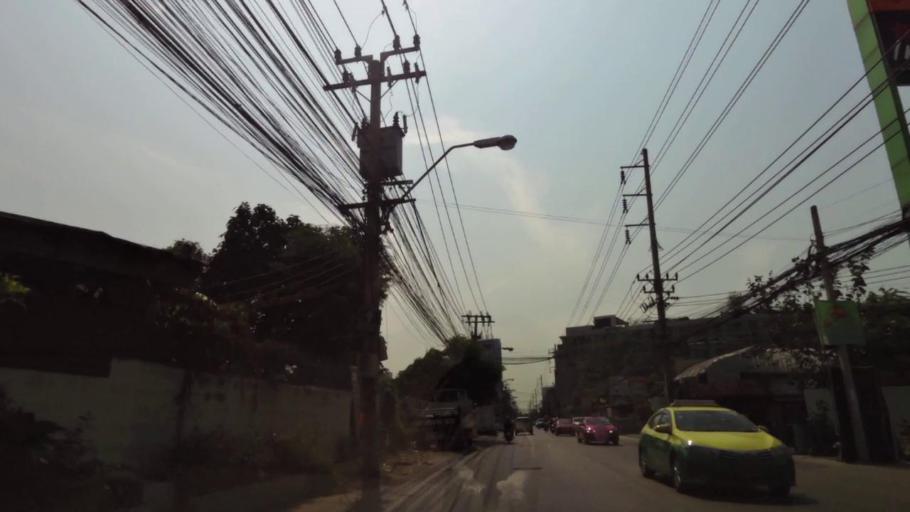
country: TH
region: Bangkok
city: Phra Khanong
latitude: 13.6545
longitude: 100.5930
